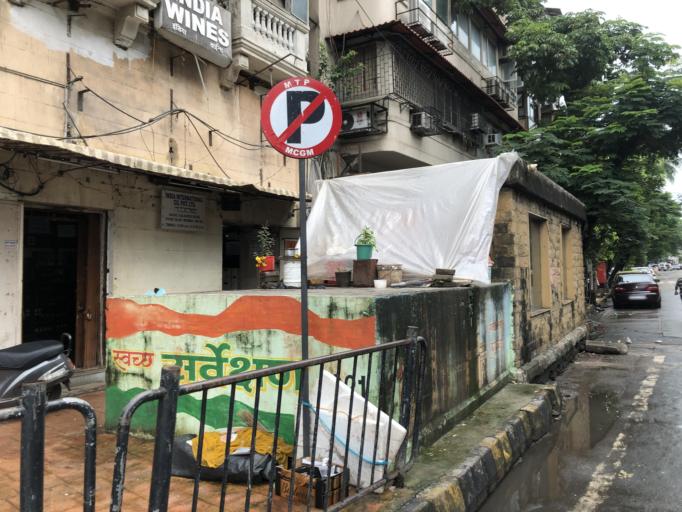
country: IN
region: Maharashtra
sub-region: Raigarh
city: Uran
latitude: 18.9442
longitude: 72.8295
